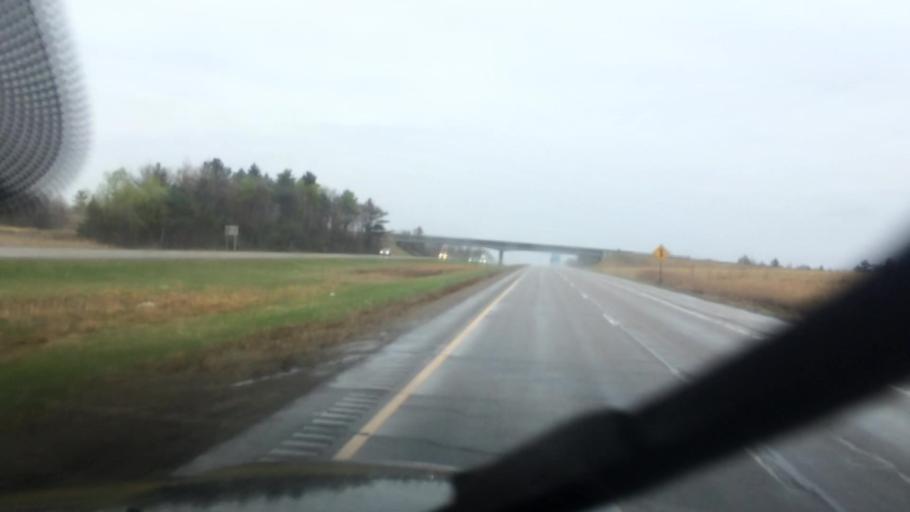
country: US
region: Wisconsin
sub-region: Portage County
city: Stevens Point
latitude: 44.5977
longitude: -89.6155
